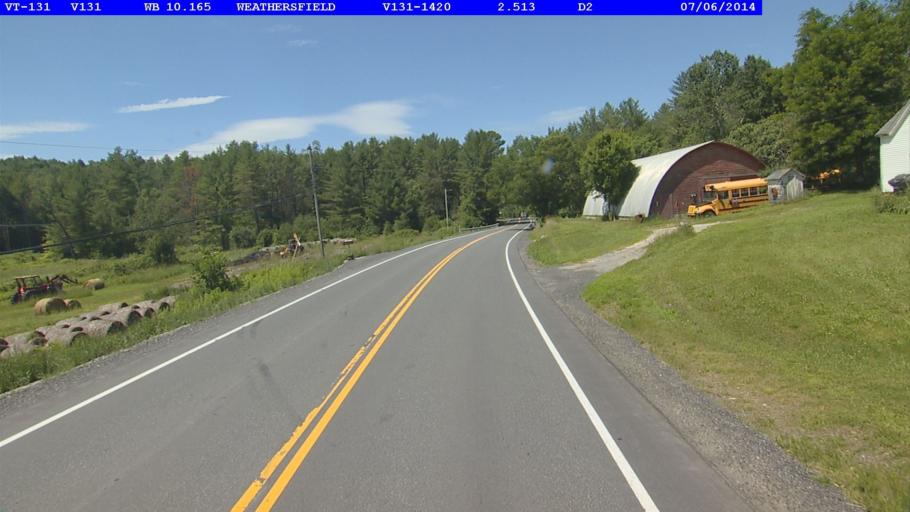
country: US
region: Vermont
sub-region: Windsor County
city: Springfield
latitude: 43.4092
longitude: -72.4989
